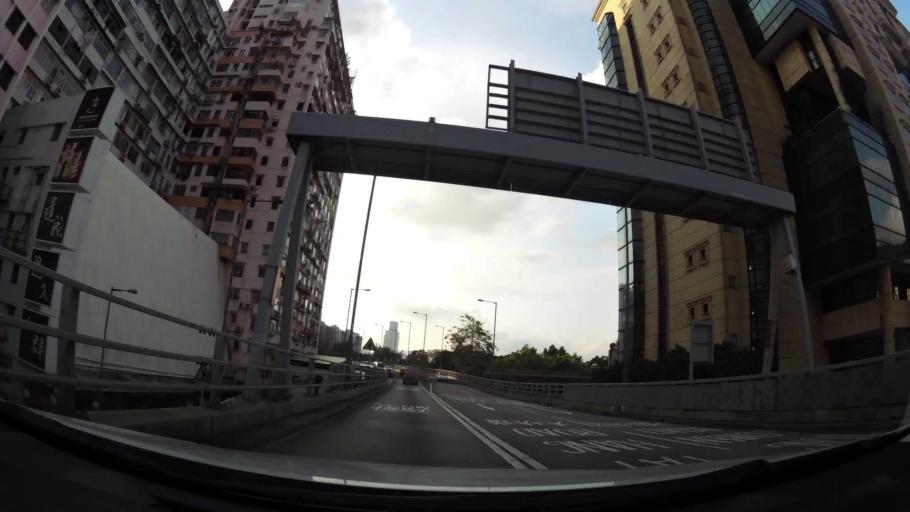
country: HK
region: Wanchai
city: Wan Chai
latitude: 22.2794
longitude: 114.1894
